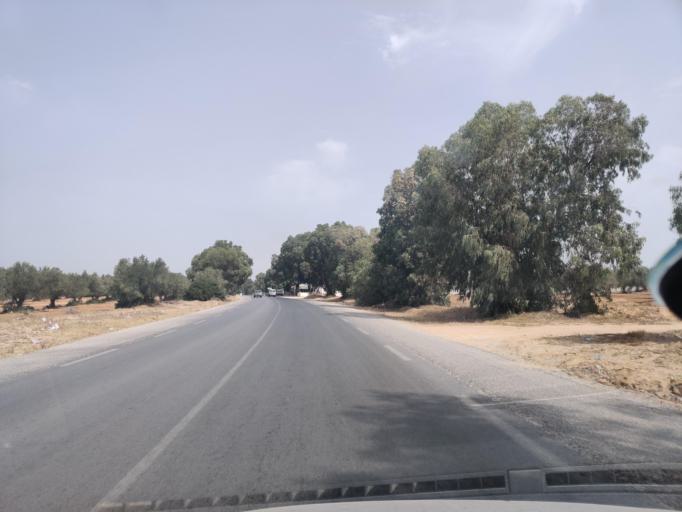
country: TN
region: Nabul
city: Al Hammamat
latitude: 36.4543
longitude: 10.5716
